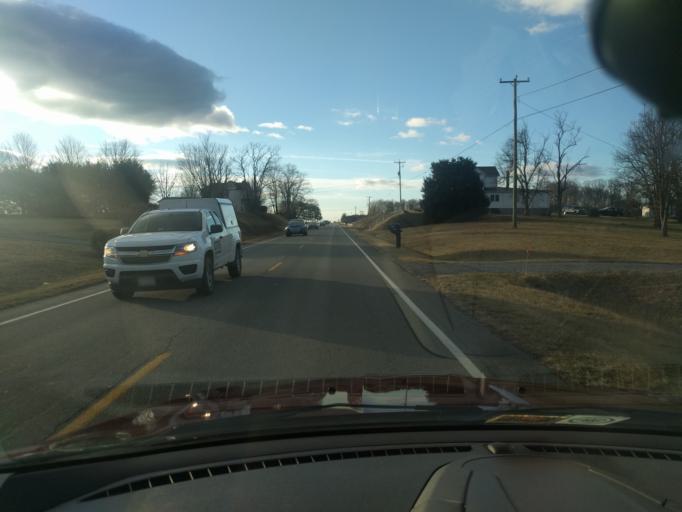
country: US
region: Virginia
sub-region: City of Bedford
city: Bedford
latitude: 37.2683
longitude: -79.5523
